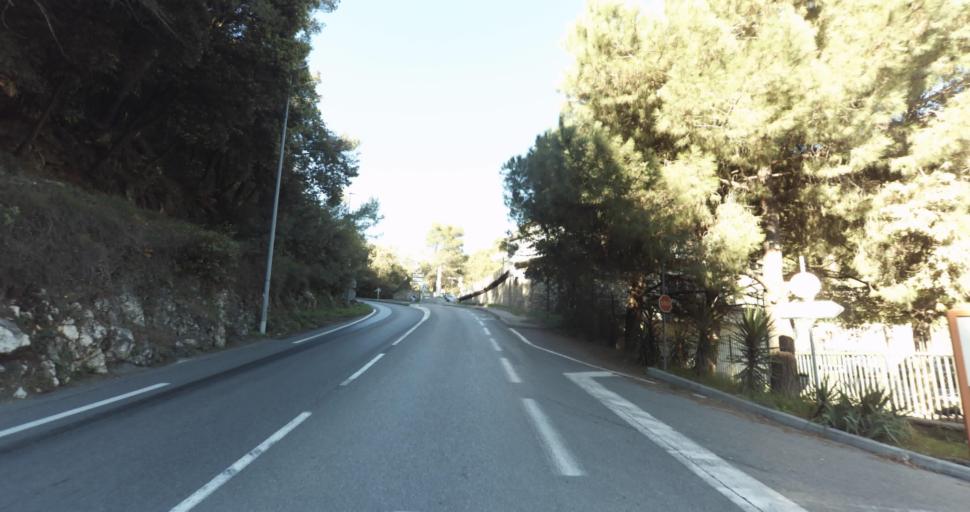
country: FR
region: Provence-Alpes-Cote d'Azur
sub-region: Departement des Alpes-Maritimes
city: Vence
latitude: 43.7146
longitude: 7.1175
